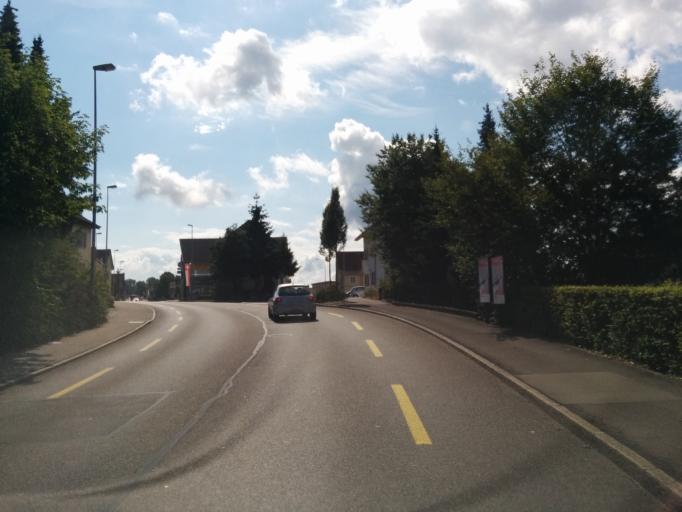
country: CH
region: Aargau
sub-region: Bezirk Bremgarten
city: Wohlen
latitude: 47.3491
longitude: 8.2831
